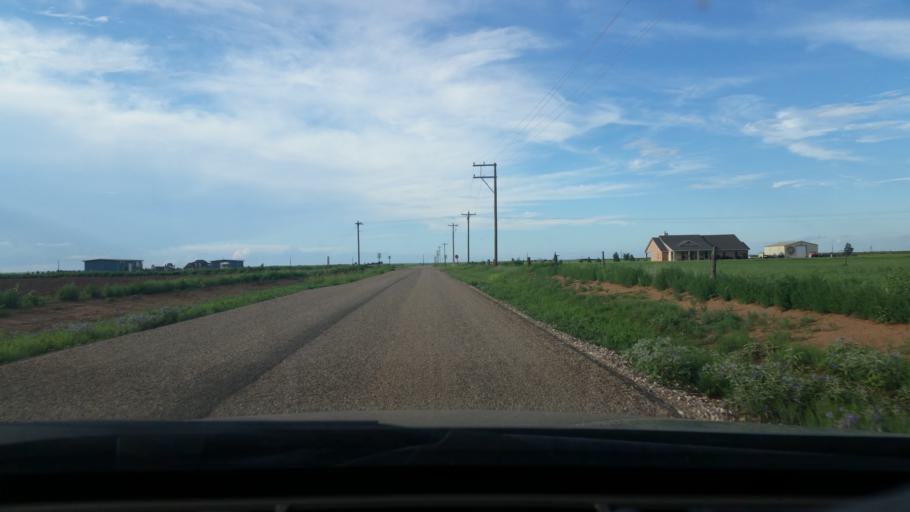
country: US
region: New Mexico
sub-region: Curry County
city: Clovis
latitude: 34.4907
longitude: -103.1788
